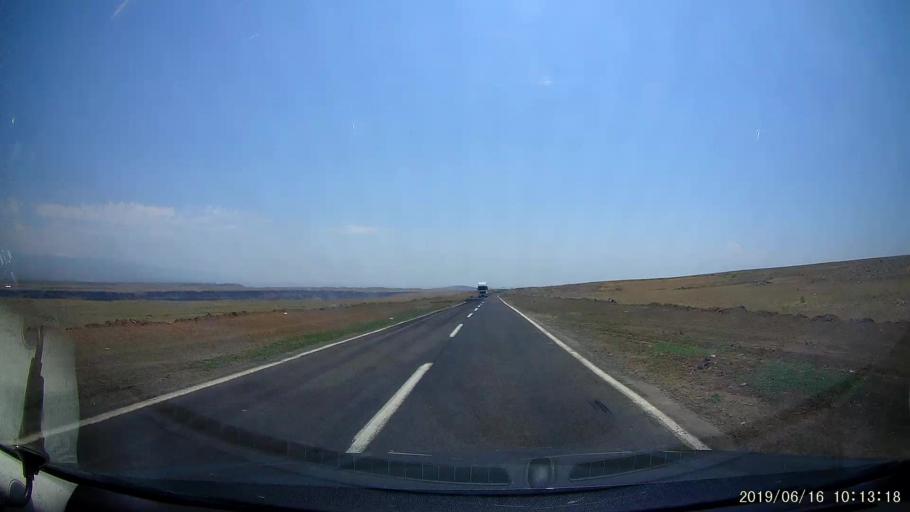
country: TR
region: Igdir
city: Tuzluca
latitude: 40.1931
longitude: 43.6396
